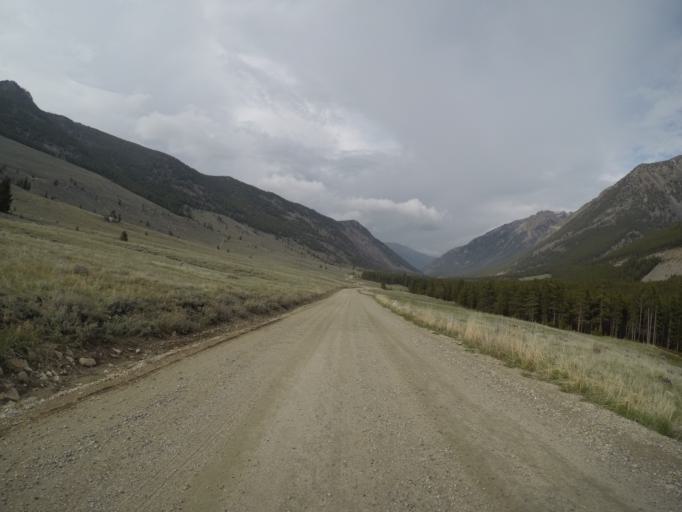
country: US
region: Montana
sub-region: Carbon County
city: Red Lodge
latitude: 45.0533
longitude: -109.4197
